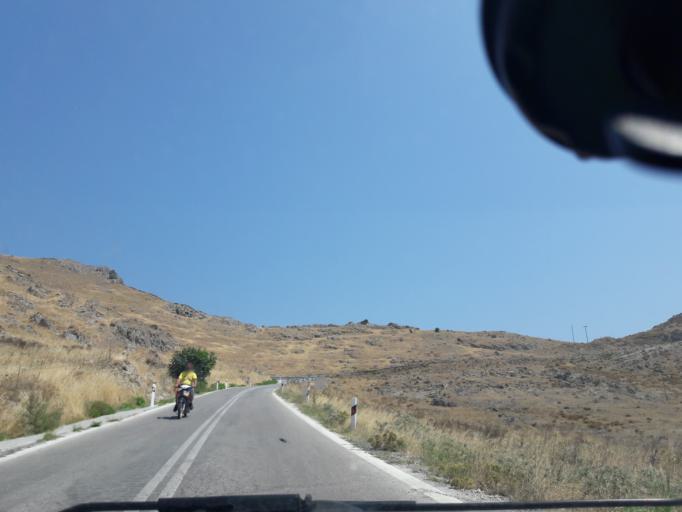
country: GR
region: North Aegean
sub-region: Nomos Lesvou
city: Myrina
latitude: 39.8637
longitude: 25.0758
